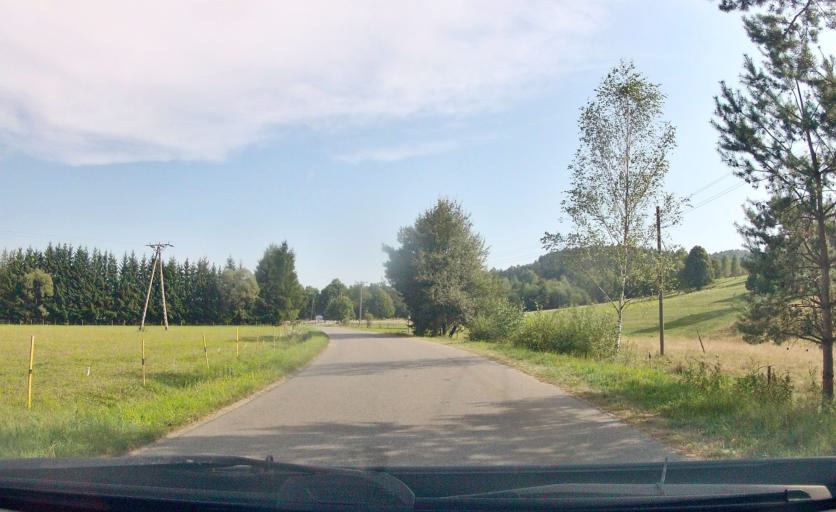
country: PL
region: Subcarpathian Voivodeship
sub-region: Powiat jasielski
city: Krempna
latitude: 49.5031
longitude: 21.5407
